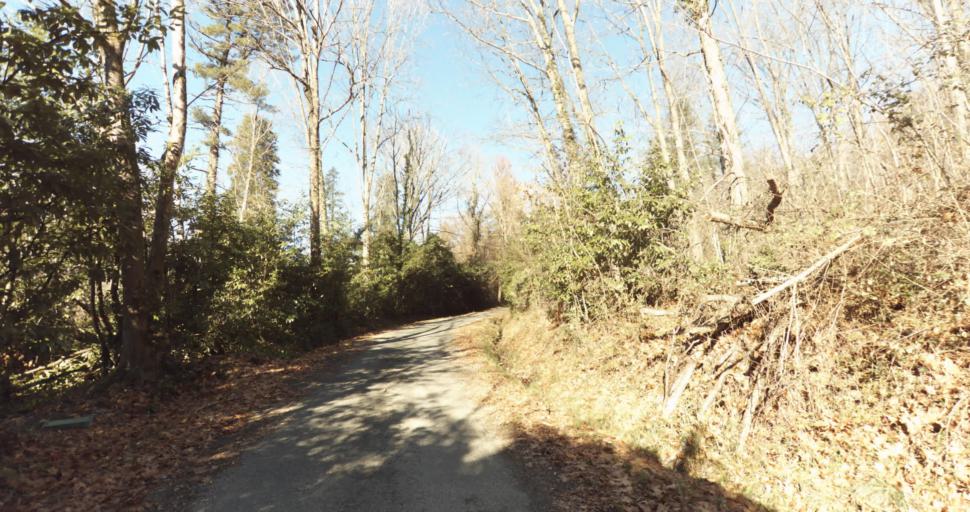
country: FR
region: Aquitaine
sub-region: Departement des Pyrenees-Atlantiques
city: Morlaas
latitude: 43.3325
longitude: -0.2817
